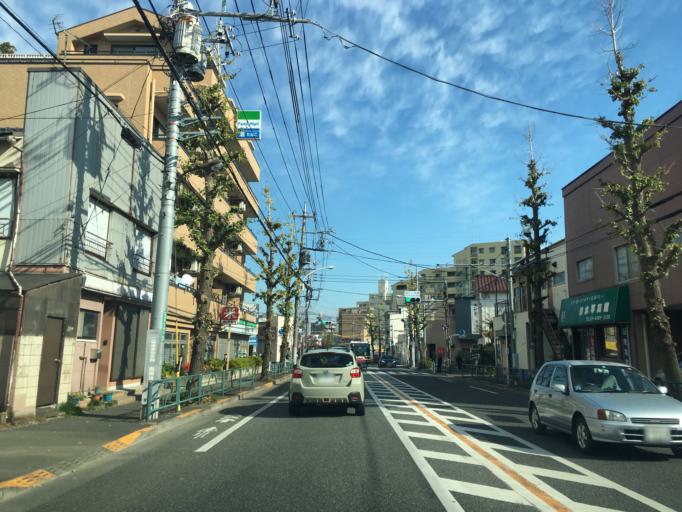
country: JP
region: Tokyo
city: Chofugaoka
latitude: 35.6313
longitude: 139.5814
